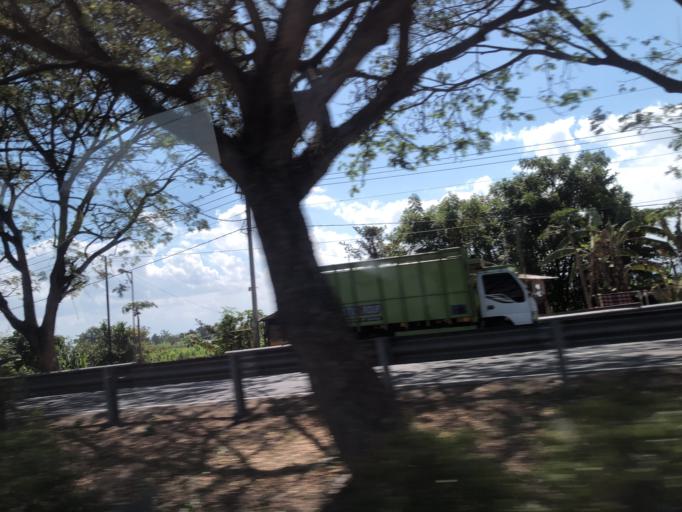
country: ID
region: Bali
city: Semarapura
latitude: -8.5671
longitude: 115.4126
